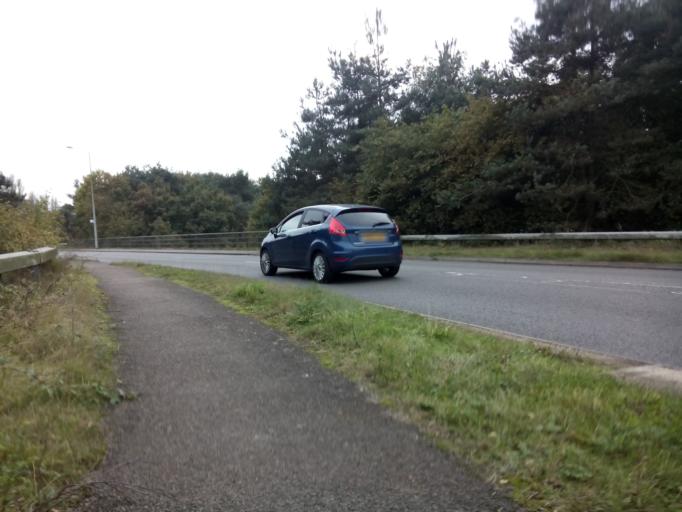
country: GB
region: England
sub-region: Suffolk
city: Ipswich
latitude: 52.0248
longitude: 1.1395
